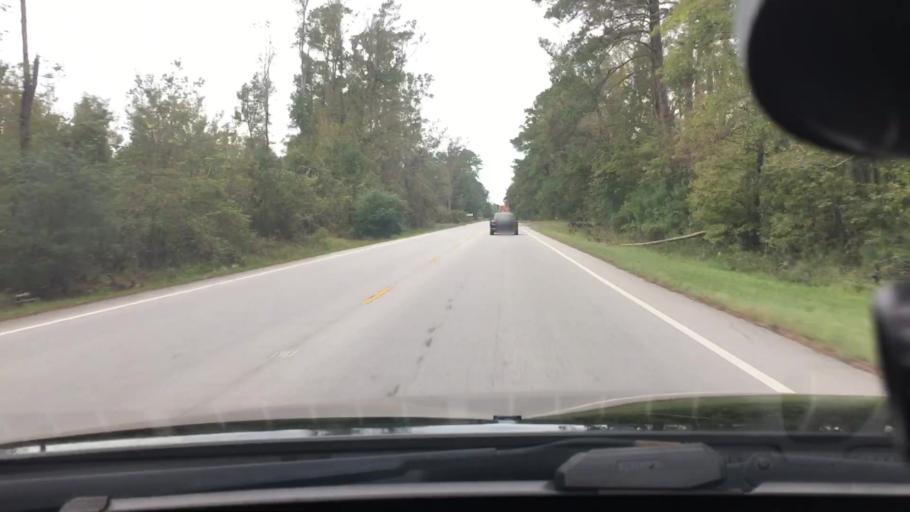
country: US
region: North Carolina
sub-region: Craven County
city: New Bern
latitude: 35.1653
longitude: -77.0405
